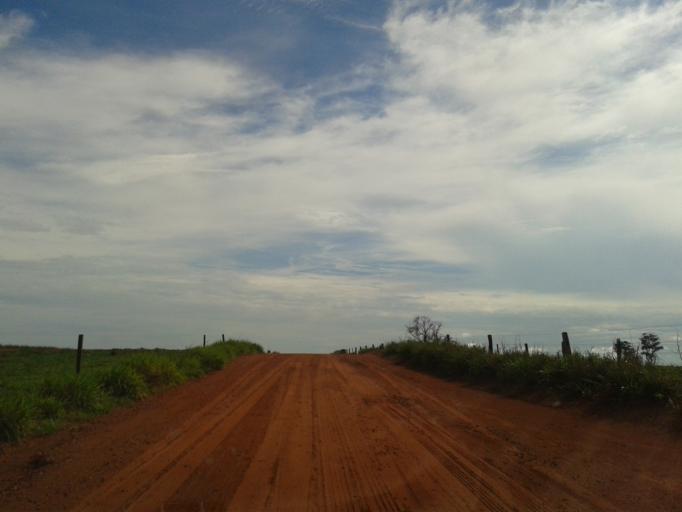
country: BR
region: Minas Gerais
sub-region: Santa Vitoria
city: Santa Vitoria
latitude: -19.2036
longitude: -50.6555
